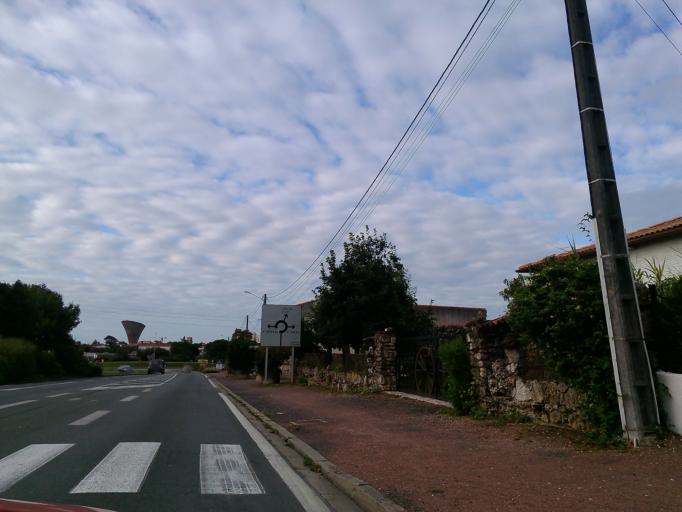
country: FR
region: Poitou-Charentes
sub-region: Departement de la Charente-Maritime
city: Royan
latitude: 45.6412
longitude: -1.0249
